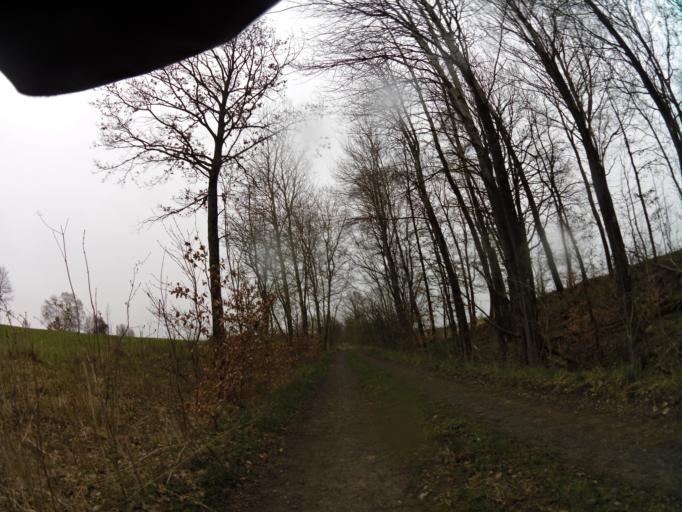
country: PL
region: West Pomeranian Voivodeship
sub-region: Powiat koszalinski
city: Bobolice
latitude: 53.9865
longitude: 16.6574
